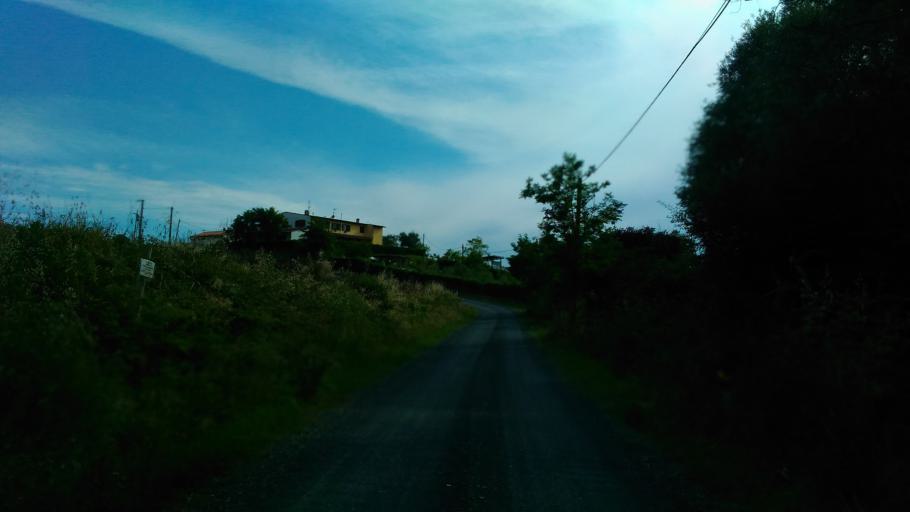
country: IT
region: Tuscany
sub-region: Province of Pisa
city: Orciano Pisano
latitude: 43.4494
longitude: 10.5218
